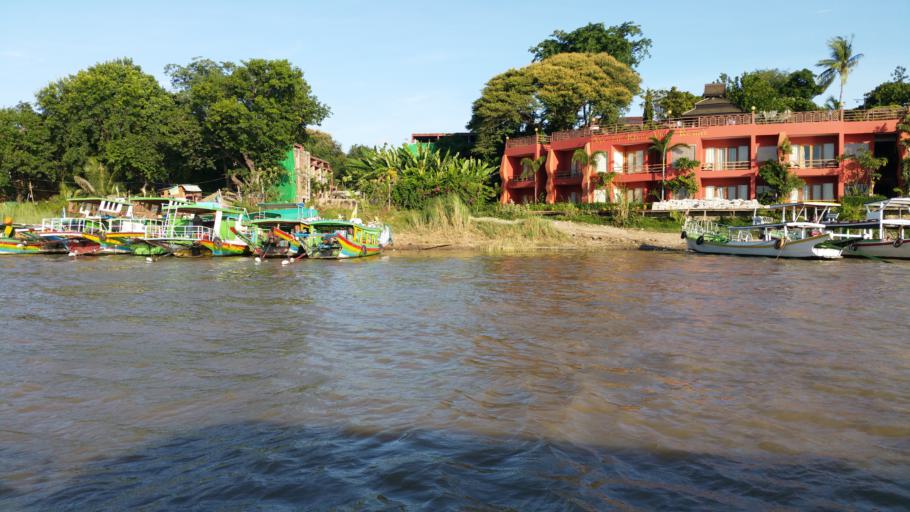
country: MM
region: Magway
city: Pakokku
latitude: 21.1796
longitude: 94.8602
